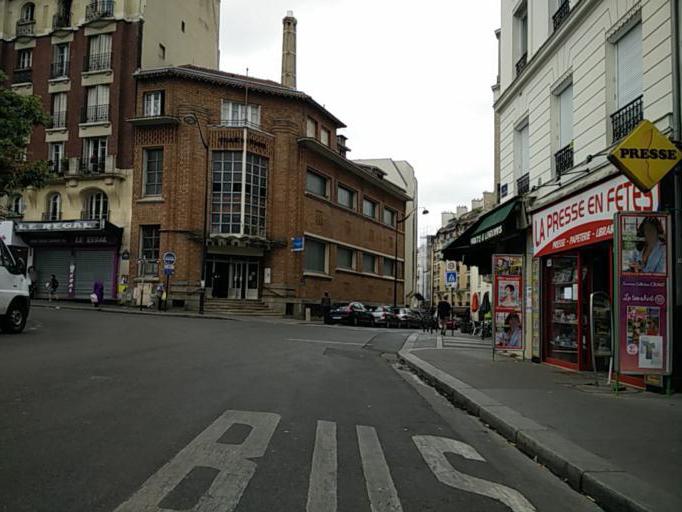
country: FR
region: Ile-de-France
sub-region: Departement de Seine-Saint-Denis
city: Le Pre-Saint-Gervais
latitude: 48.8769
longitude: 2.3925
